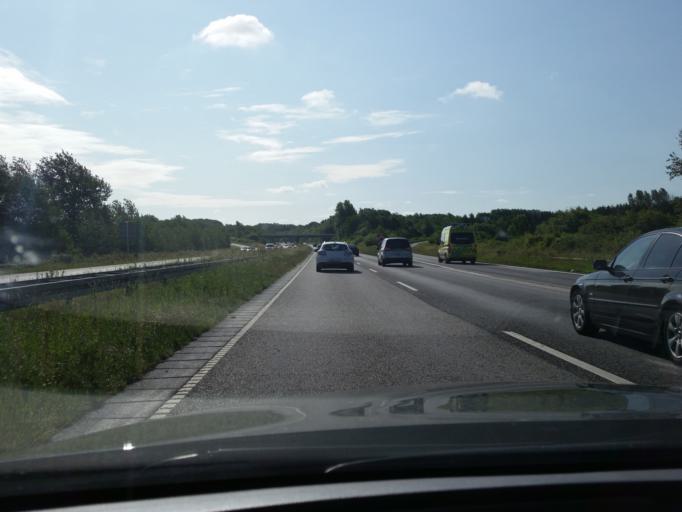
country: DK
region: South Denmark
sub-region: Assens Kommune
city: Tommerup Stationsby
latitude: 55.3899
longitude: 10.2039
